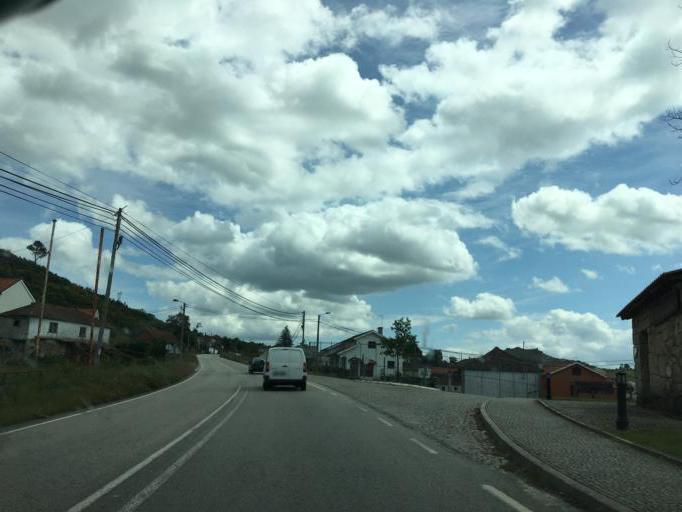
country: PT
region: Vila Real
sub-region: Boticas
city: Boticas
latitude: 41.6937
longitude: -7.6532
